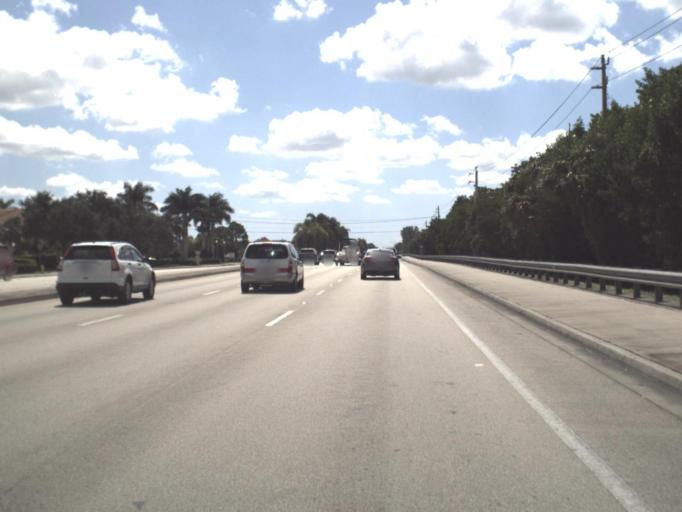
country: US
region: Florida
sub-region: Collier County
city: Naples Park
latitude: 26.2893
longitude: -81.8021
